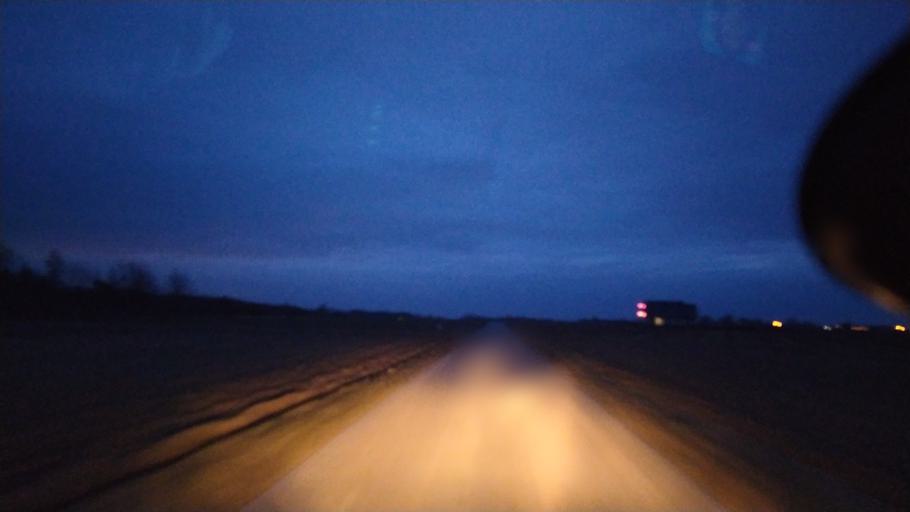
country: PL
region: Lublin Voivodeship
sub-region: Powiat lubelski
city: Jastkow
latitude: 51.3594
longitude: 22.4054
